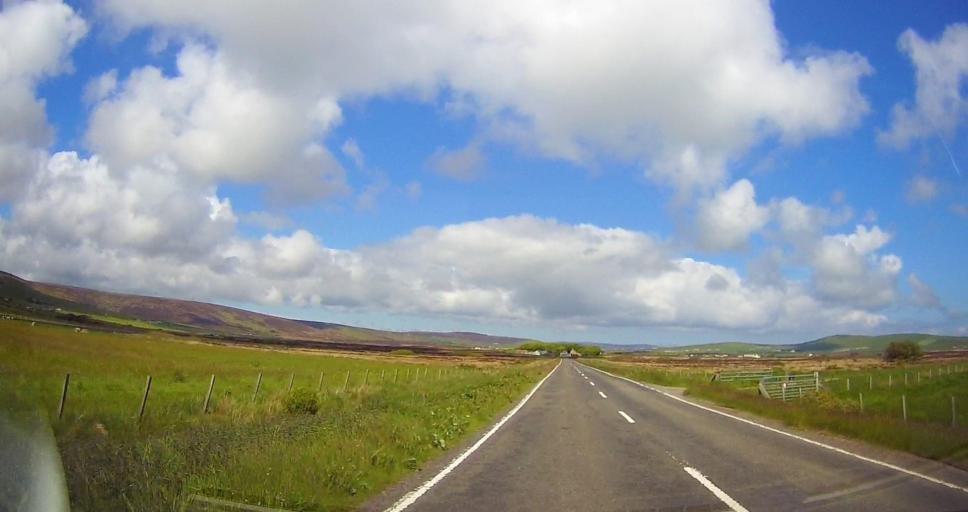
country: GB
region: Scotland
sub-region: Orkney Islands
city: Orkney
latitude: 59.0400
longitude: -3.0871
